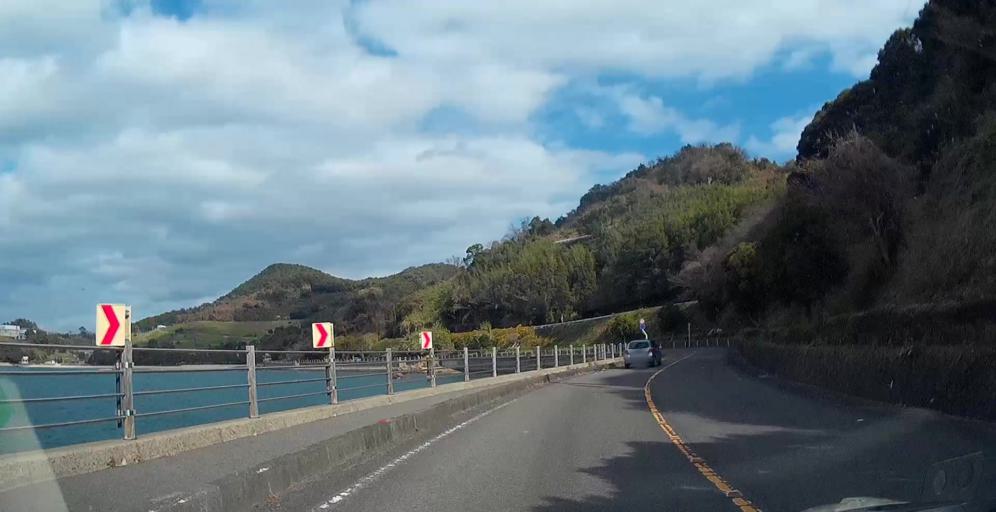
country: JP
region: Kumamoto
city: Minamata
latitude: 32.3134
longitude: 130.4701
